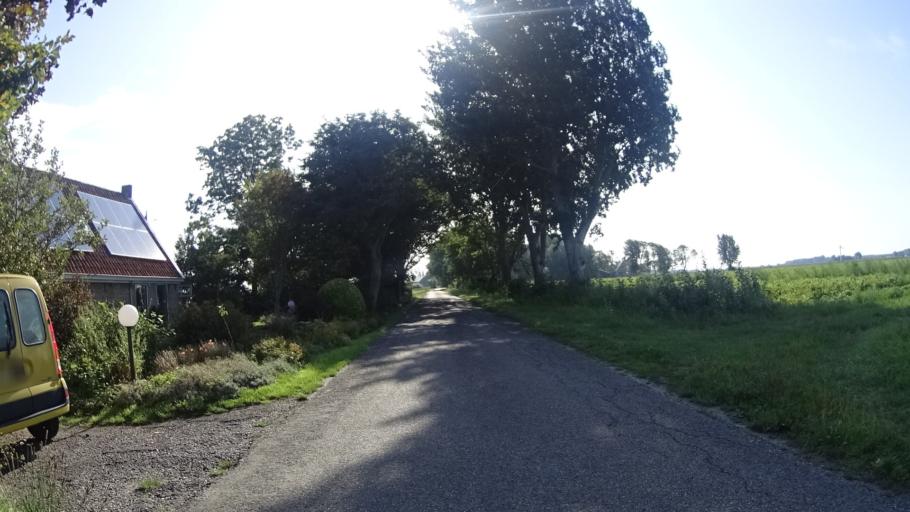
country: NL
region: Friesland
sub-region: Gemeente Harlingen
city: Harlingen
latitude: 53.1225
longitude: 5.4493
